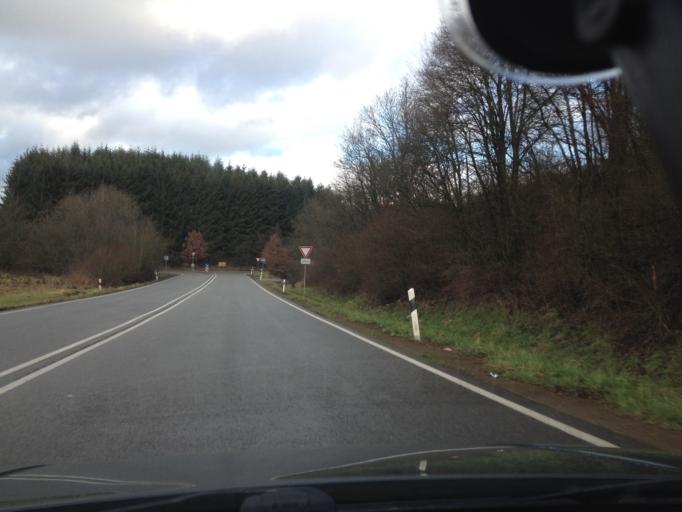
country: DE
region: Saarland
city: Namborn
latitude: 49.5038
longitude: 7.1482
